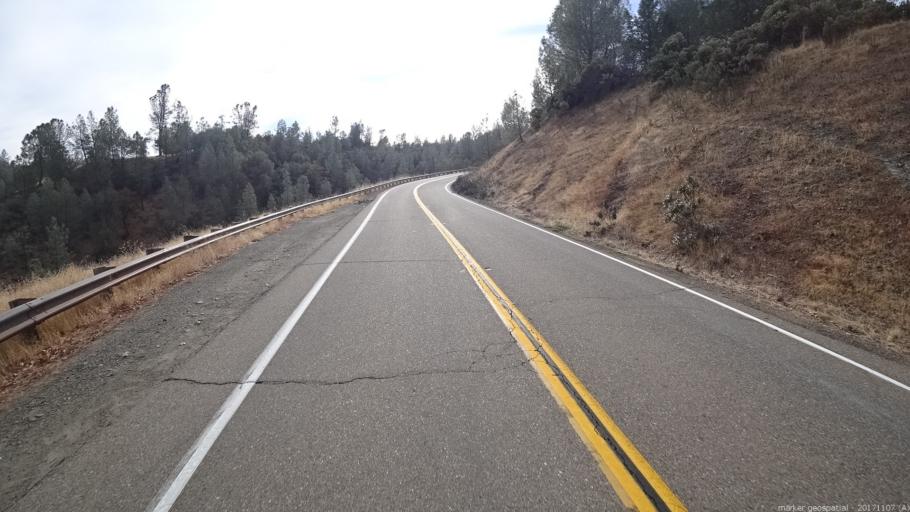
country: US
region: California
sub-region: Shasta County
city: Shasta
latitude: 40.5103
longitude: -122.5239
